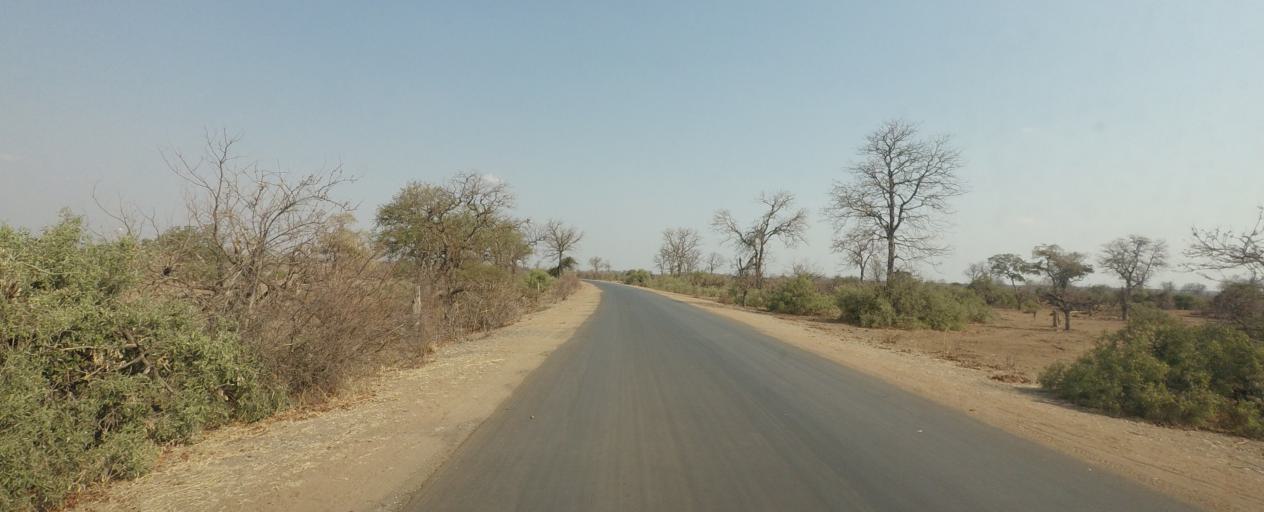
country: ZA
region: Limpopo
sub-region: Mopani District Municipality
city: Giyani
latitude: -23.1026
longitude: 31.4275
